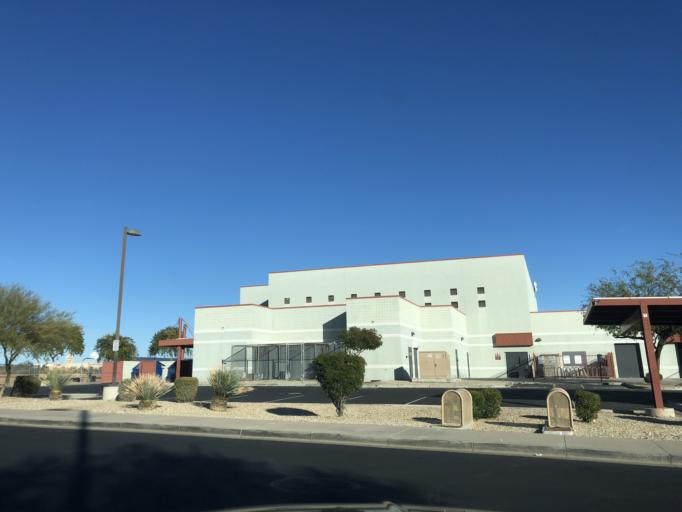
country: US
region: Arizona
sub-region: Maricopa County
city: Buckeye
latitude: 33.4386
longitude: -112.5639
